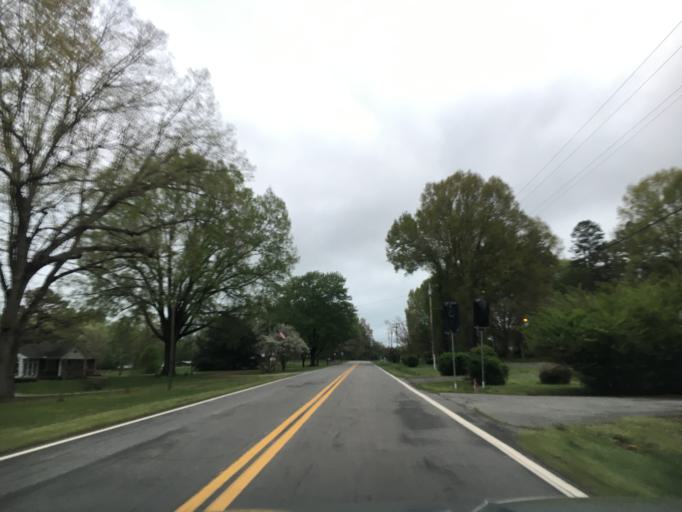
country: US
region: Virginia
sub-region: Halifax County
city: South Boston
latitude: 36.6599
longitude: -78.8800
